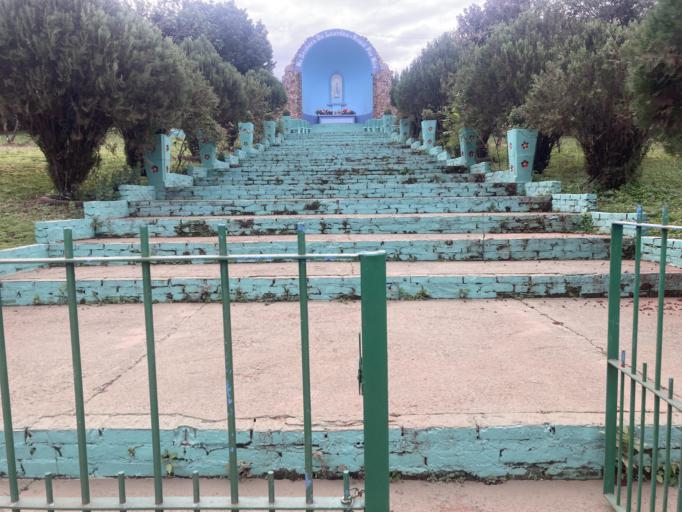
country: BR
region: Rio Grande do Sul
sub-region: Sao Pedro Do Butia
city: Butia Inferior
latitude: -27.9819
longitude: -54.8588
